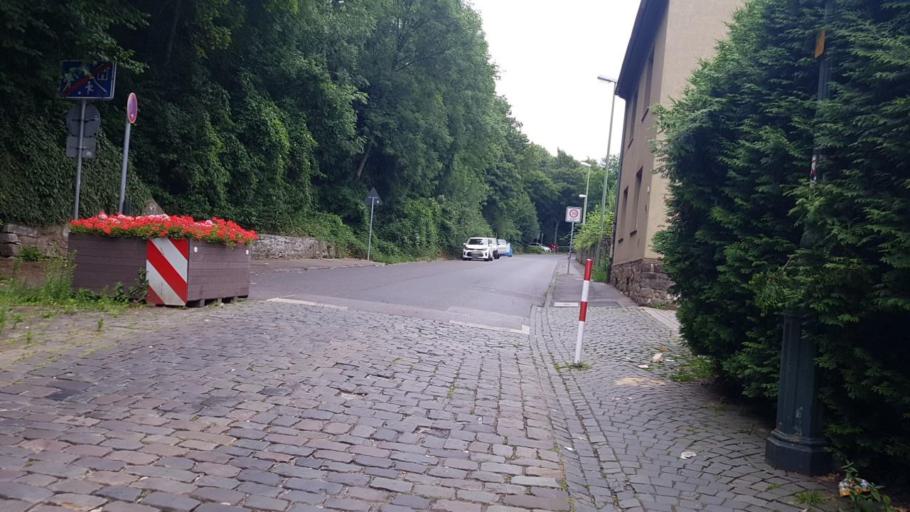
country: DE
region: North Rhine-Westphalia
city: Stolberg
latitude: 50.7685
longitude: 6.2368
